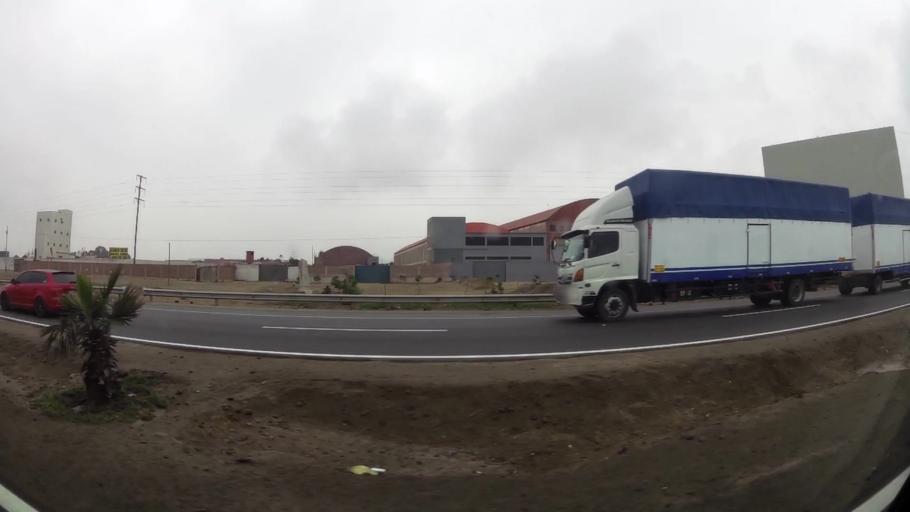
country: PE
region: Lima
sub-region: Lima
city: Punta Hermosa
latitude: -12.3132
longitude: -76.8335
